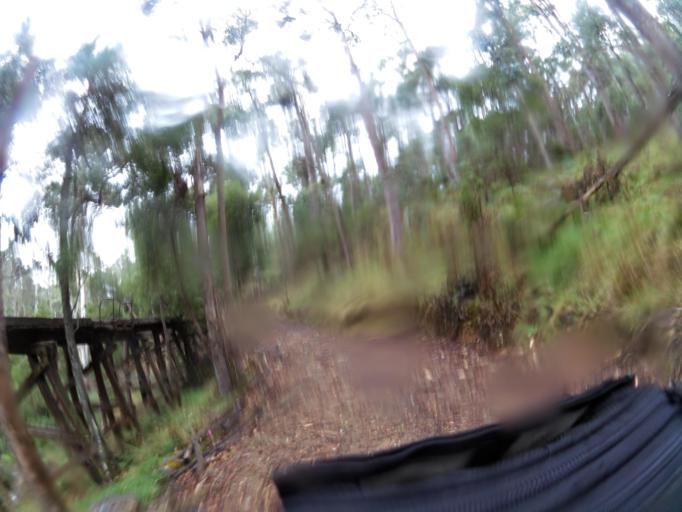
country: AU
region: New South Wales
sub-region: Greater Hume Shire
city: Holbrook
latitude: -36.1651
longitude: 147.4851
